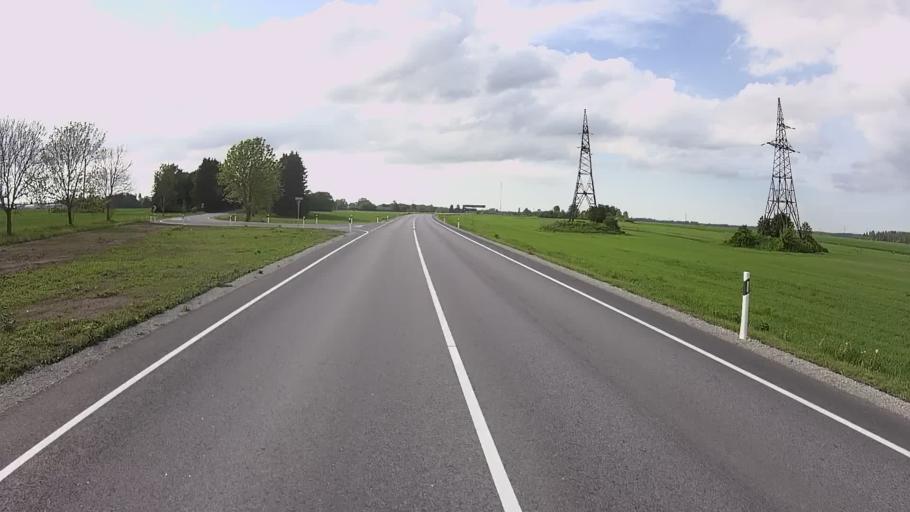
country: EE
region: Laeaene-Virumaa
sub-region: Vinni vald
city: Vinni
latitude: 59.2399
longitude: 26.4892
